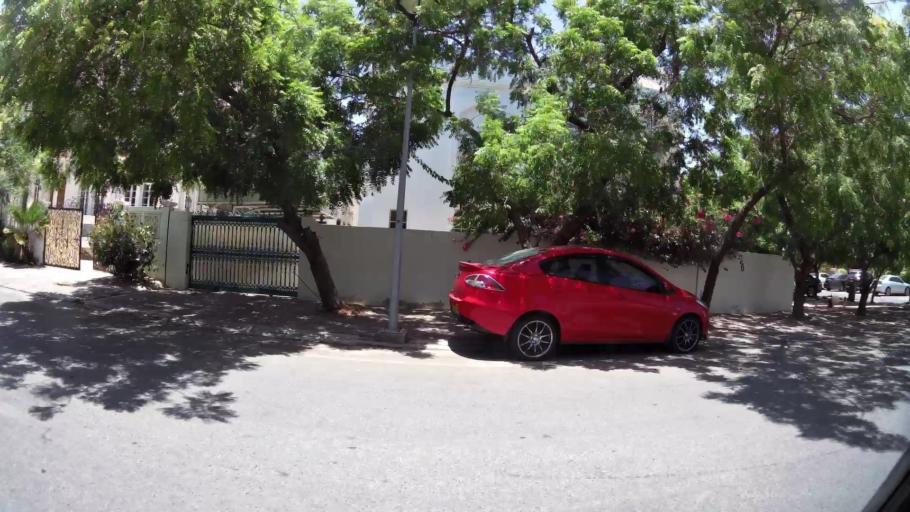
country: OM
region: Muhafazat Masqat
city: Bawshar
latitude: 23.6021
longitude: 58.4033
